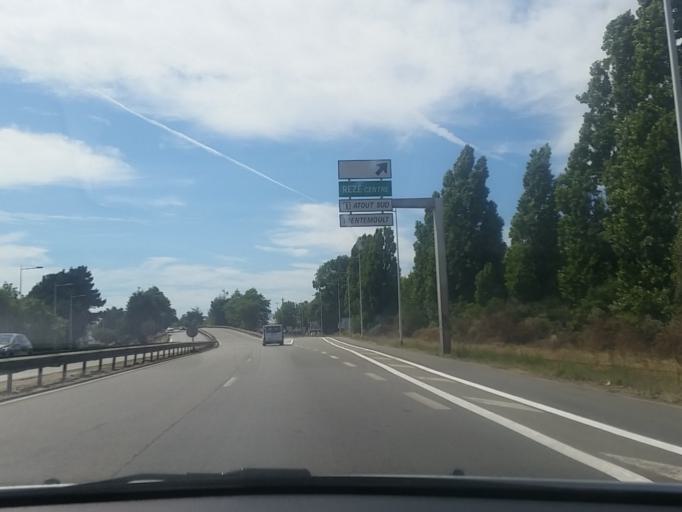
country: FR
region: Pays de la Loire
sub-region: Departement de la Loire-Atlantique
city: Reze
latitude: 47.1930
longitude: -1.5665
